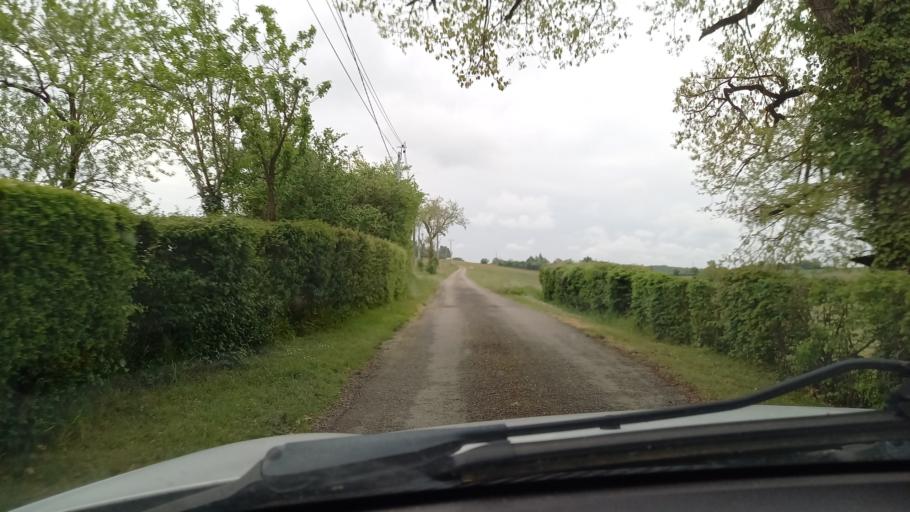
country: FR
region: Midi-Pyrenees
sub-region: Departement du Gers
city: Aubiet
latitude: 43.7604
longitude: 0.8431
